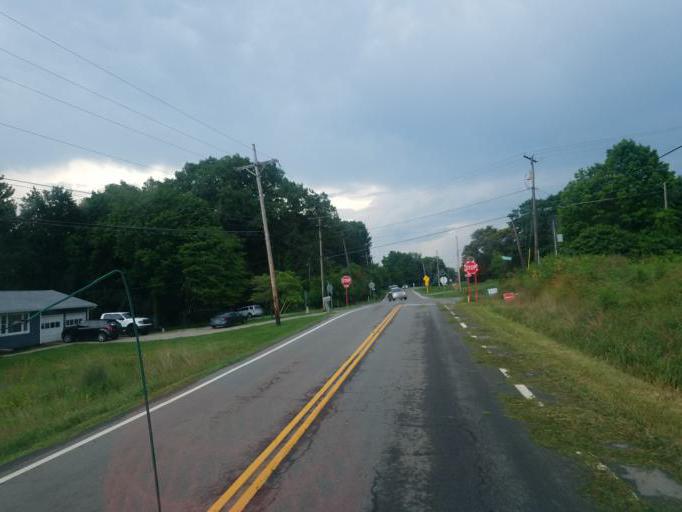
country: US
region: Ohio
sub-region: Wayne County
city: Doylestown
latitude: 40.9720
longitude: -81.7368
